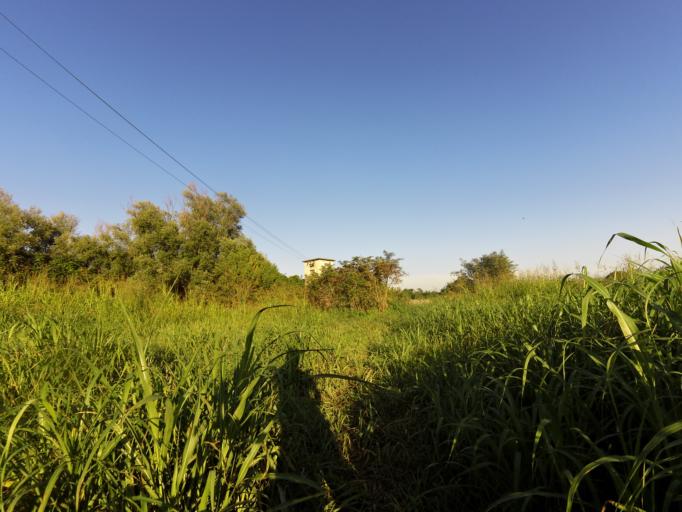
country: IT
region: Lombardy
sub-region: Citta metropolitana di Milano
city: Civesio
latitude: 45.3989
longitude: 9.2738
